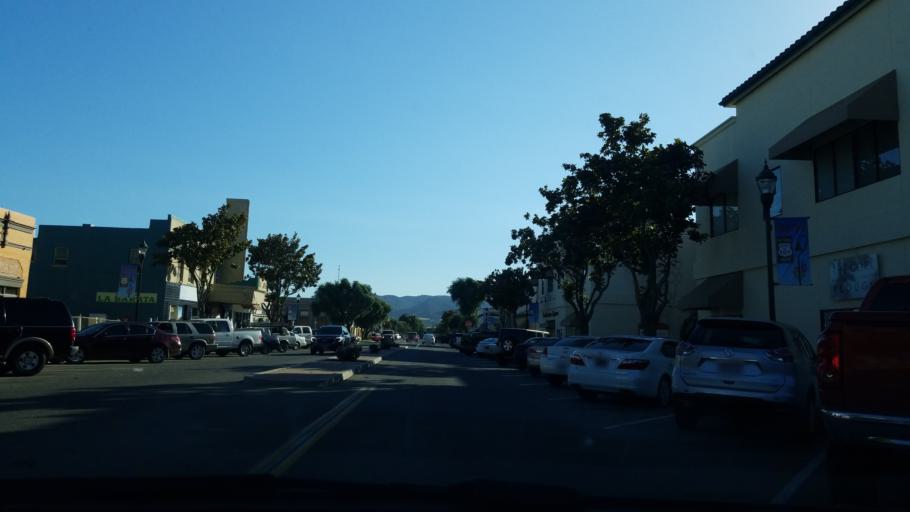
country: US
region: California
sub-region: Monterey County
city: King City
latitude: 36.2135
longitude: -121.1253
